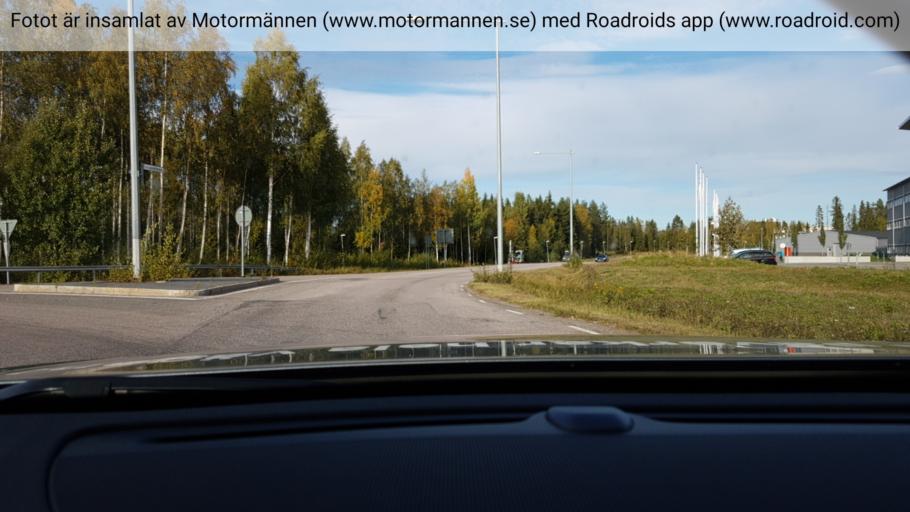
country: SE
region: Norrbotten
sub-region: Lulea Kommun
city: Bergnaset
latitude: 65.6124
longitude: 22.1178
